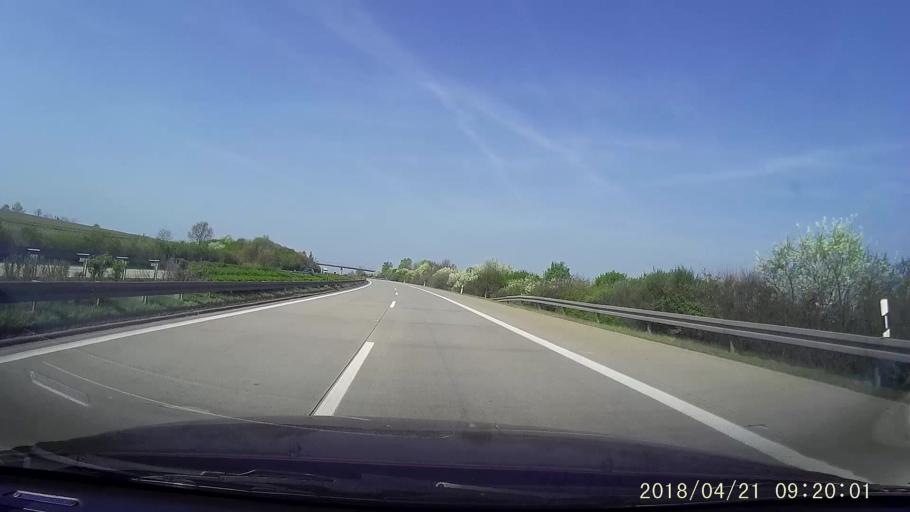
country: DE
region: Saxony
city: Weissenberg
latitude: 51.2107
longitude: 14.6263
